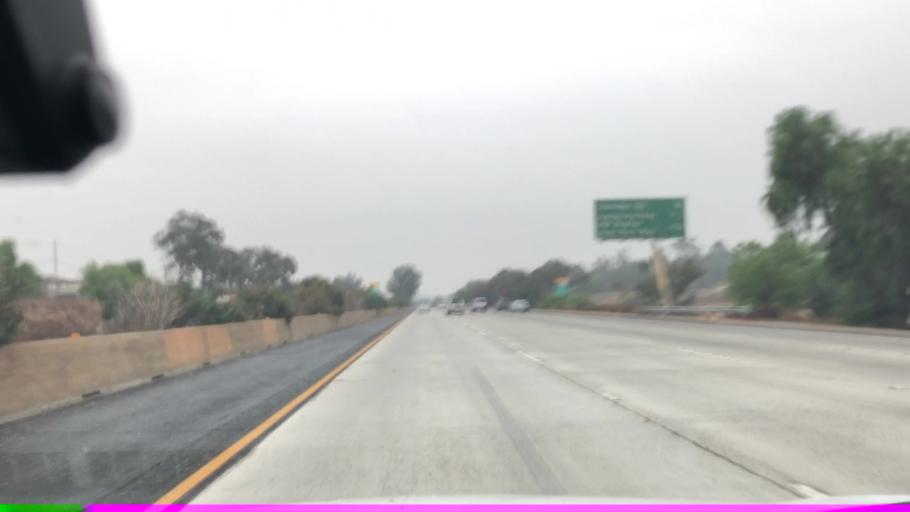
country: US
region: California
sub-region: San Diego County
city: Escondido
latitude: 33.1376
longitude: -117.1051
